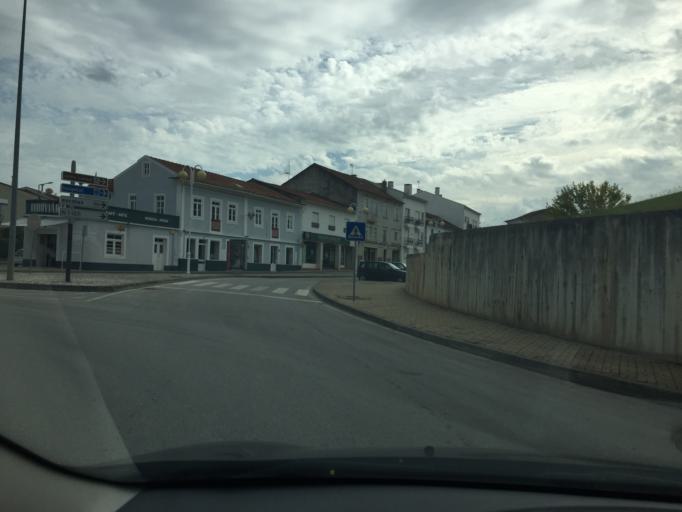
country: PT
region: Aveiro
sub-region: Anadia
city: Arcos
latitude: 40.4449
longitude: -8.4367
